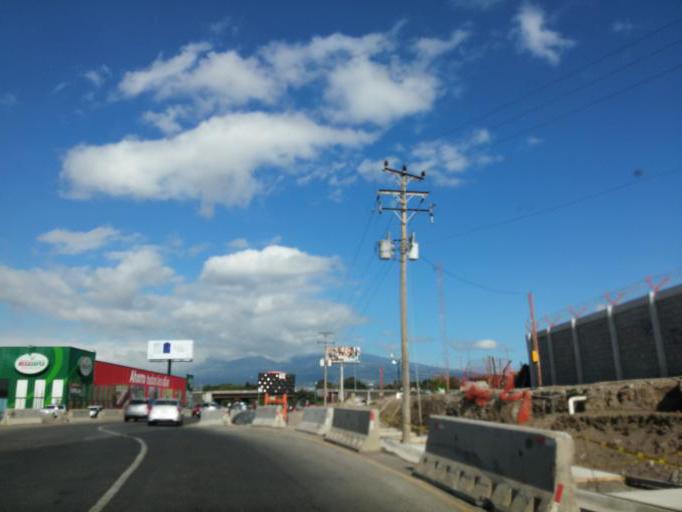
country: CR
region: San Jose
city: San Jose
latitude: 9.9125
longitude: -84.0770
